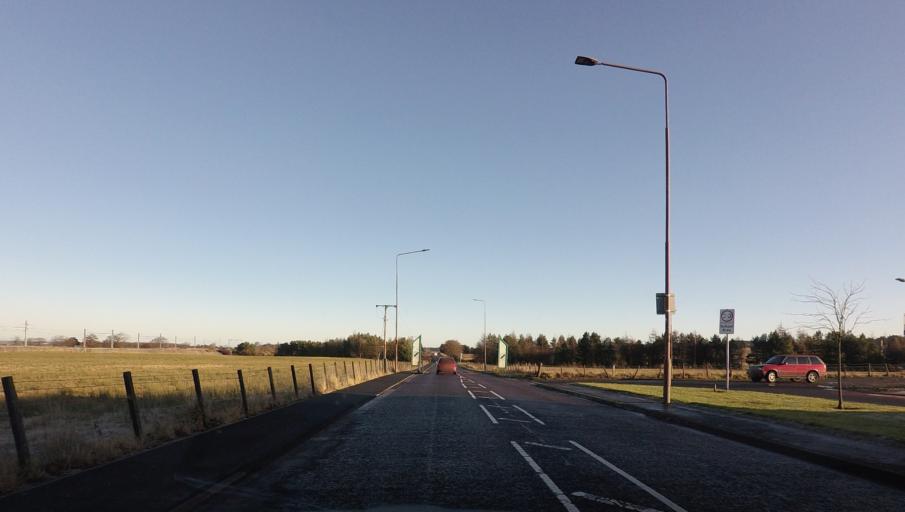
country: GB
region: Scotland
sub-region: West Lothian
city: Blackburn
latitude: 55.8310
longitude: -3.6502
